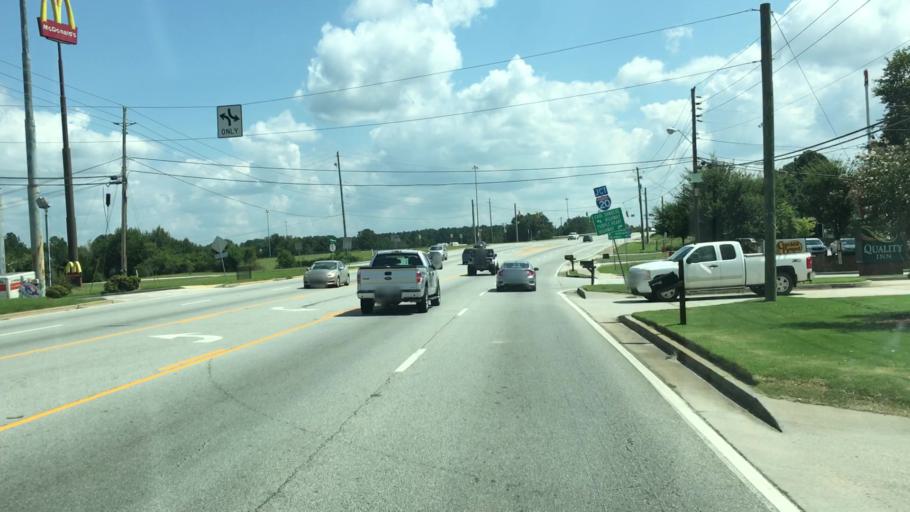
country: US
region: Georgia
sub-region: Morgan County
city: Madison
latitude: 33.5582
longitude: -83.4760
